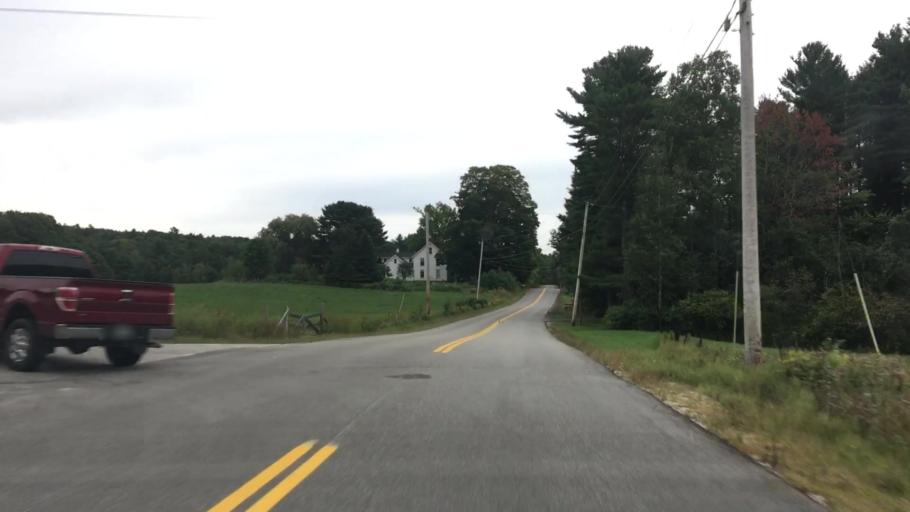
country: US
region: Maine
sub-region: Cumberland County
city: New Gloucester
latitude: 43.9184
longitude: -70.2459
